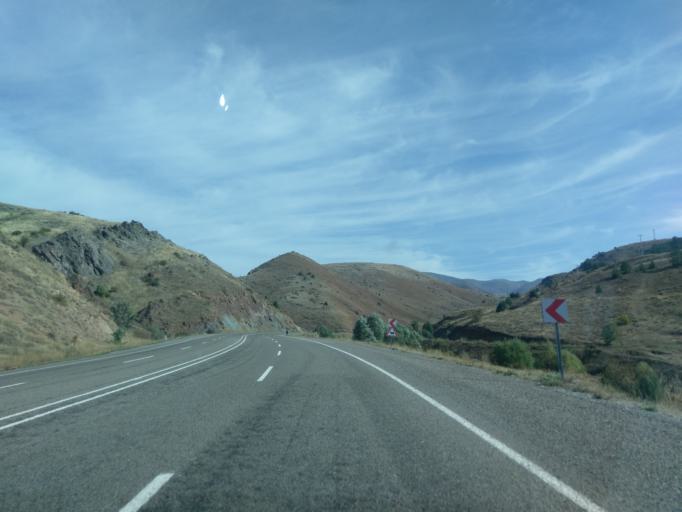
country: TR
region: Sivas
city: Imranli
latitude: 39.8488
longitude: 38.2939
